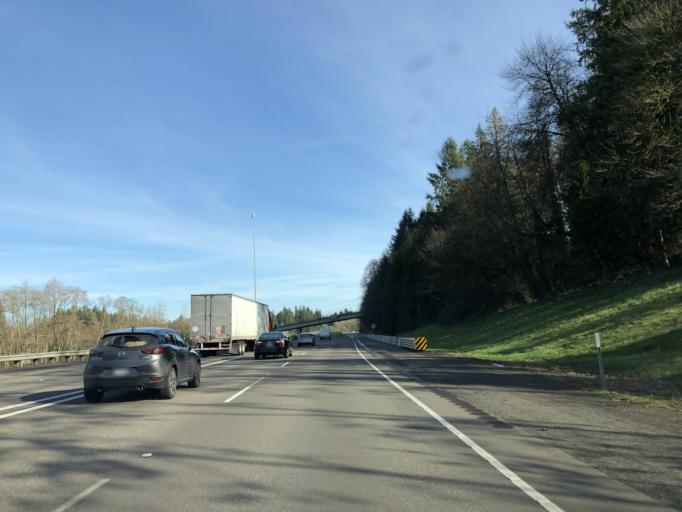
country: US
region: Oregon
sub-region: Washington County
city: Tualatin
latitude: 45.3707
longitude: -122.7474
